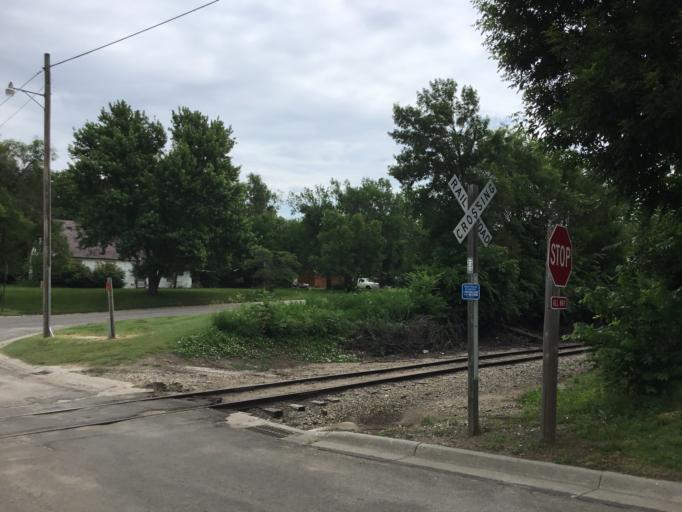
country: US
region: Kansas
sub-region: Republic County
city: Belleville
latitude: 39.8268
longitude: -97.6334
